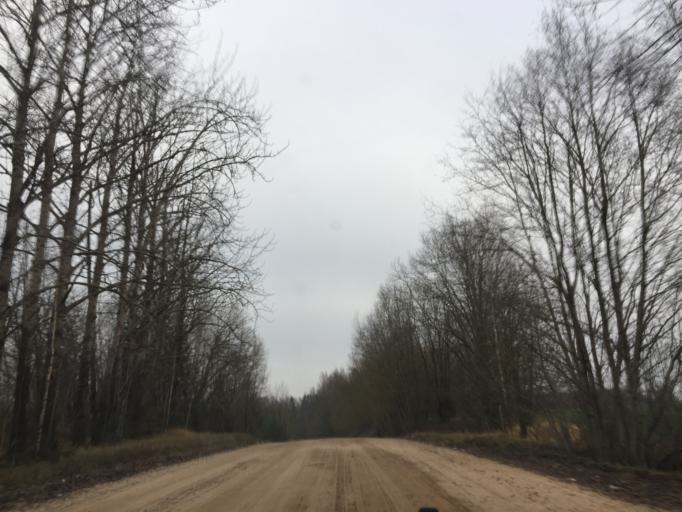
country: LV
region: Limbazu Rajons
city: Limbazi
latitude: 57.5971
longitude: 24.6169
